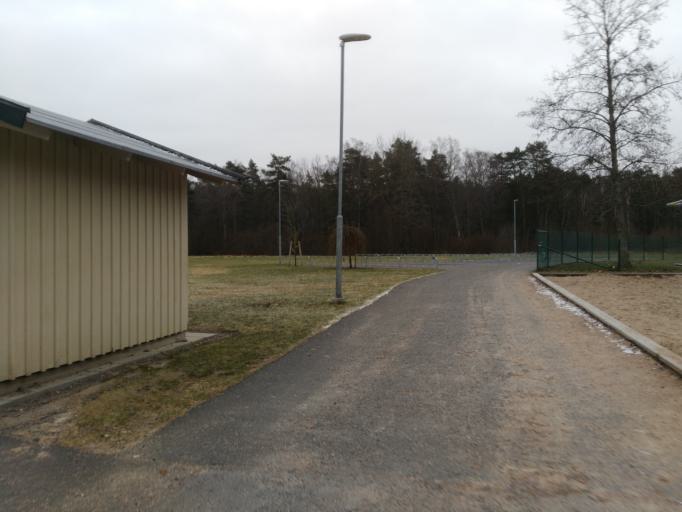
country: SE
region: Vaestra Goetaland
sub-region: Lidkopings Kommun
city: Lidkoping
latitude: 58.4895
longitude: 13.1561
